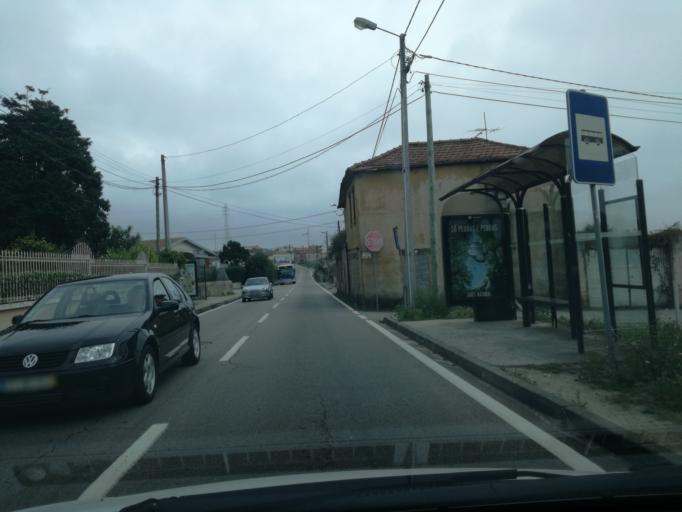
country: PT
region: Aveiro
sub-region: Espinho
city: Espinho
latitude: 40.9991
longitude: -8.6369
